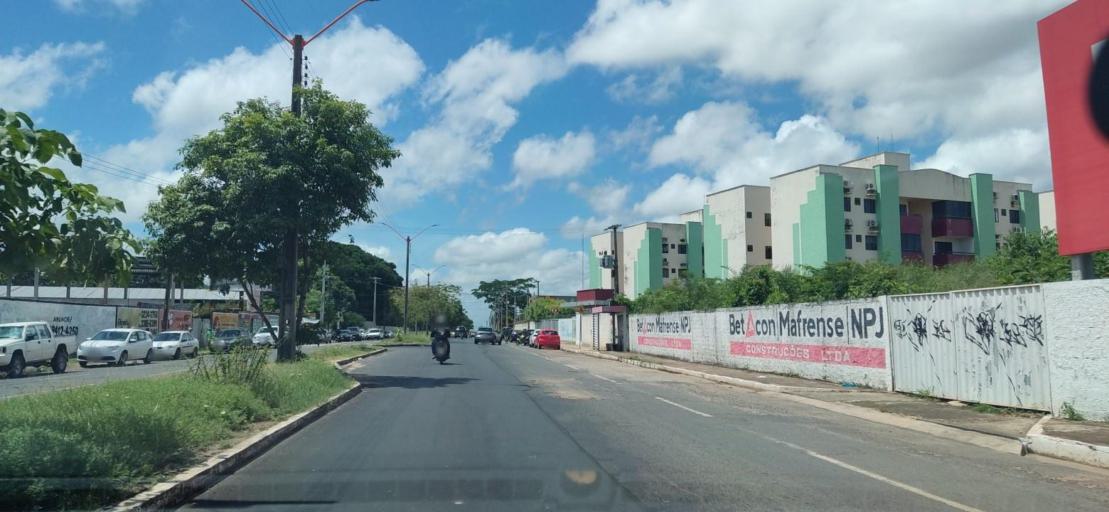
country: BR
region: Piaui
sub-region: Teresina
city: Teresina
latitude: -5.0733
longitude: -42.7499
